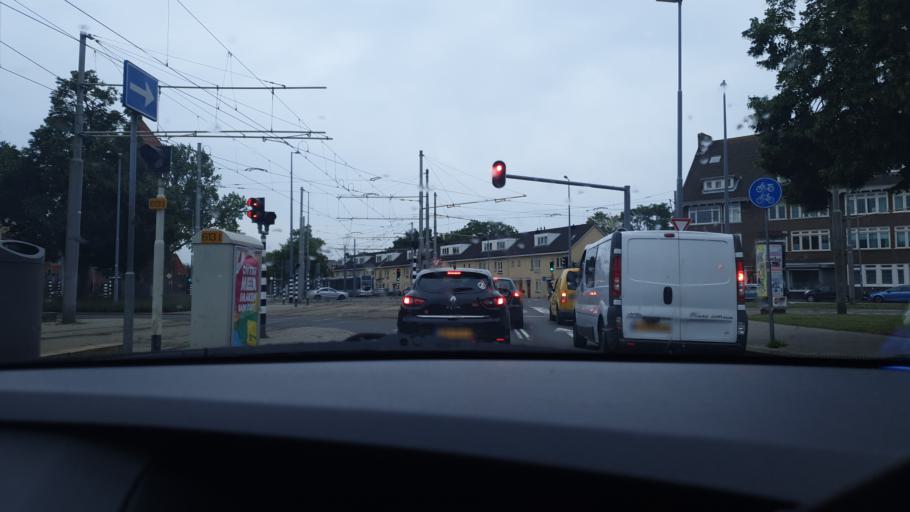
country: NL
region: South Holland
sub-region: Gemeente Barendrecht
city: Barendrecht
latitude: 51.8909
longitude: 4.5135
